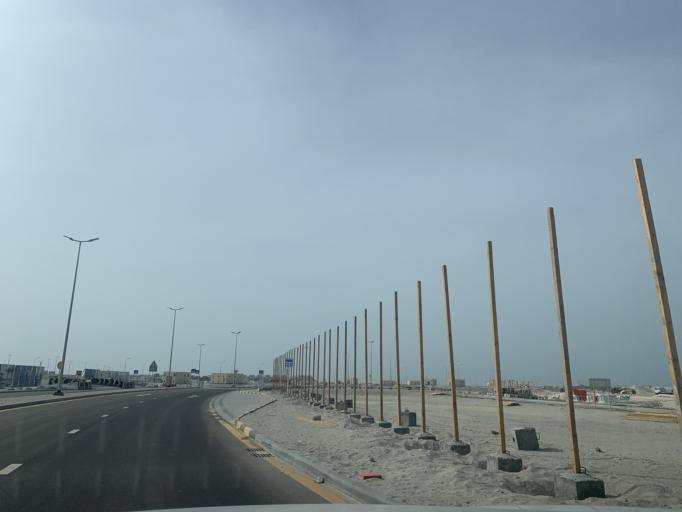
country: BH
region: Muharraq
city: Al Muharraq
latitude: 26.3153
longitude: 50.6342
